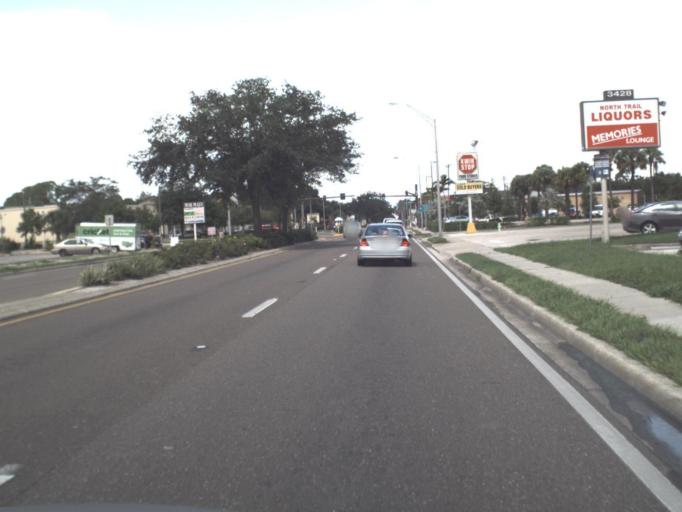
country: US
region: Florida
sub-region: Sarasota County
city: North Sarasota
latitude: 27.3655
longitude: -82.5510
